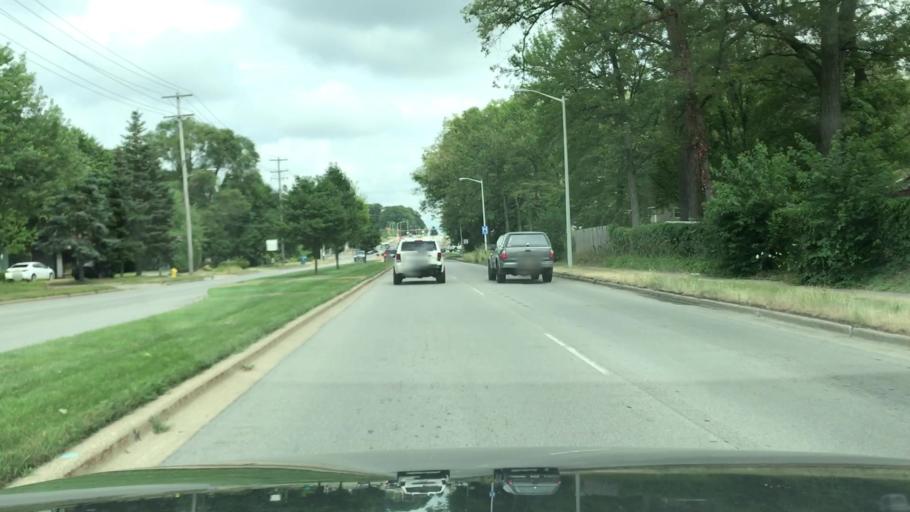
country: US
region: Michigan
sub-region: Kent County
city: Wyoming
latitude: 42.8846
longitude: -85.7268
